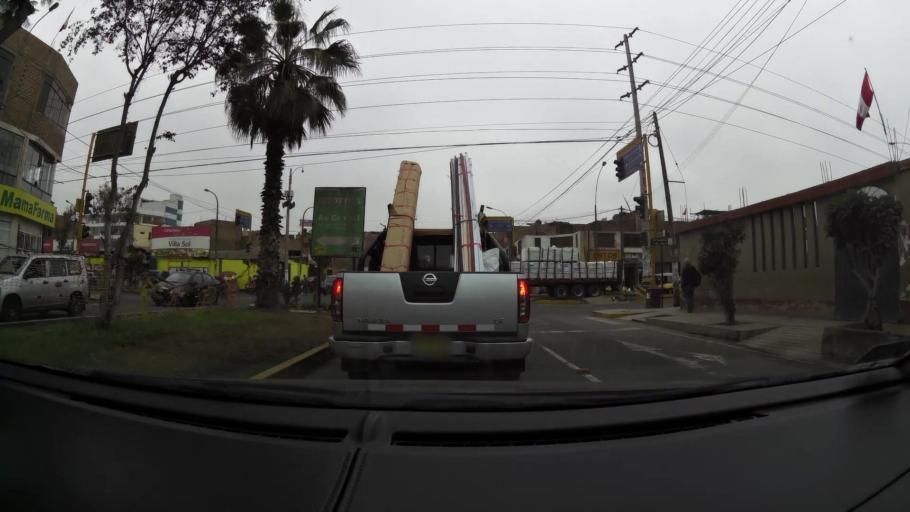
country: PE
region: Lima
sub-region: Lima
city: Independencia
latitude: -11.9595
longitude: -77.0729
